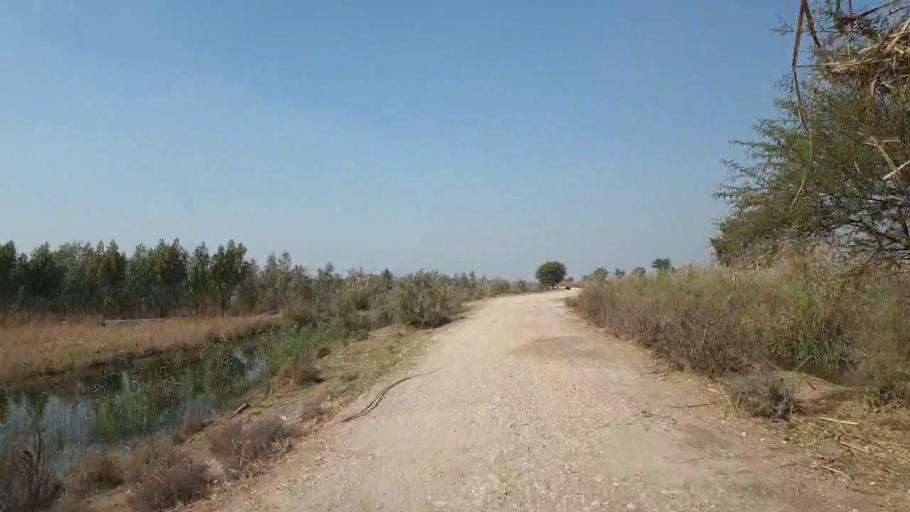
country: PK
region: Sindh
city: Bhit Shah
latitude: 25.9164
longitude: 68.5009
